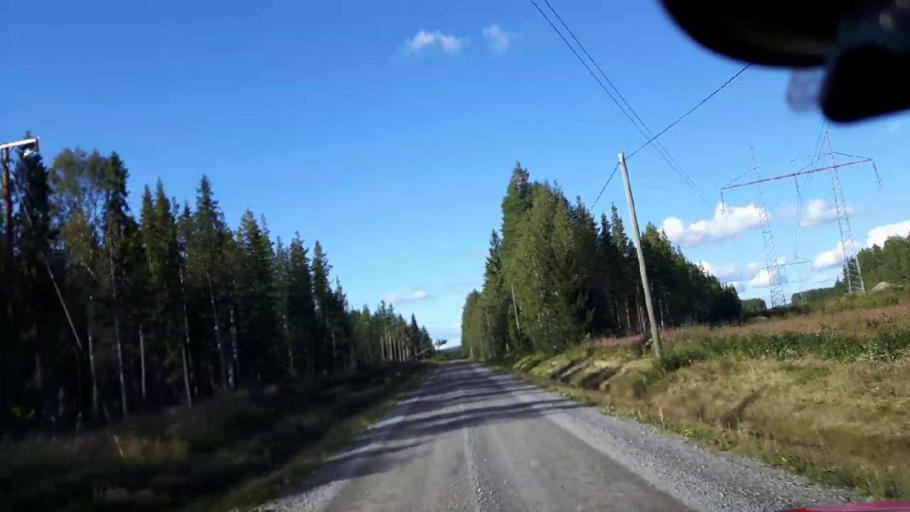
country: SE
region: Jaemtland
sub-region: Ragunda Kommun
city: Hammarstrand
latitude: 63.5173
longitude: 16.0567
